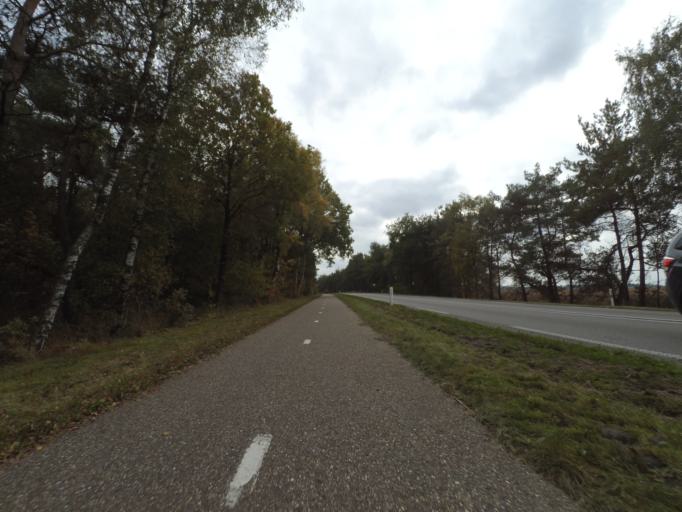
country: NL
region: Gelderland
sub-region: Gemeente Ermelo
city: Ermelo
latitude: 52.2893
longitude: 5.6835
